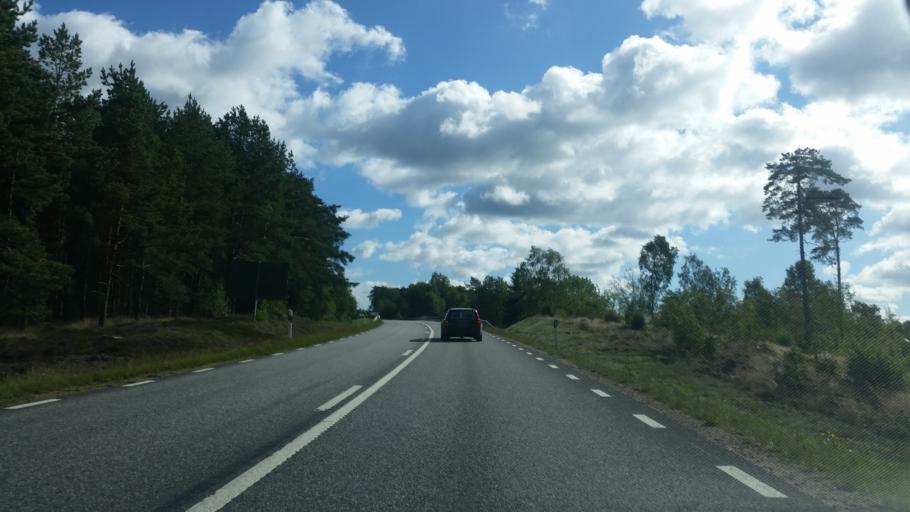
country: SE
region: Joenkoeping
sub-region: Varnamo Kommun
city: Forsheda
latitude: 57.1666
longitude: 13.8179
